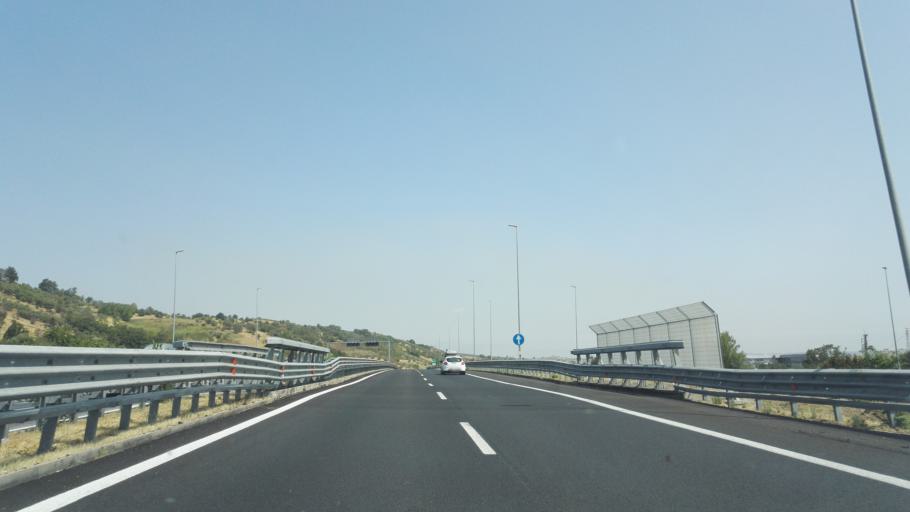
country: IT
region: Calabria
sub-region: Provincia di Cosenza
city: Sartano
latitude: 39.5070
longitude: 16.2097
